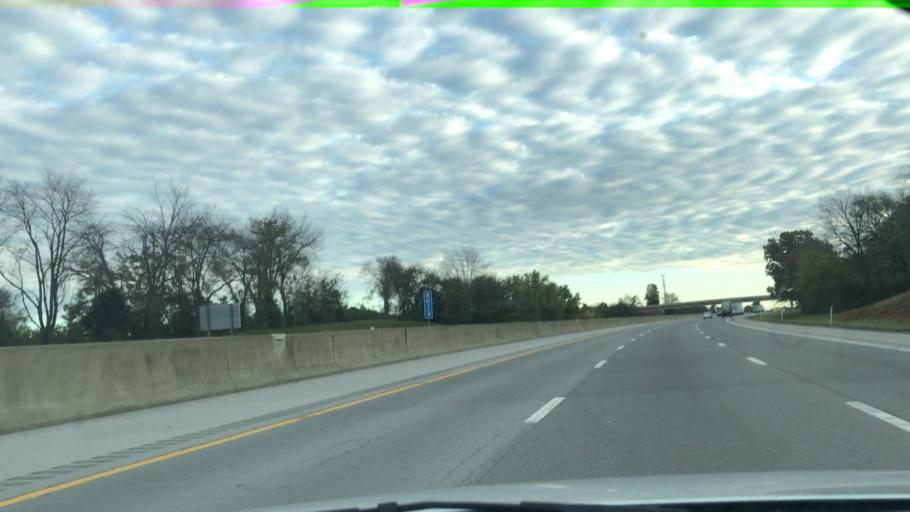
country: US
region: Kentucky
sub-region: Simpson County
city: Franklin
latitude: 36.7335
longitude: -86.5116
